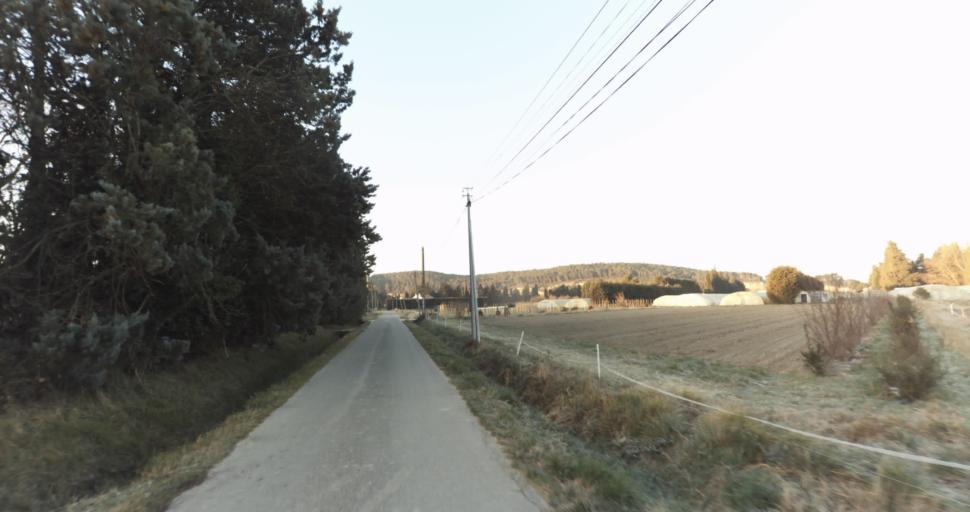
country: FR
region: Provence-Alpes-Cote d'Azur
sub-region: Departement des Bouches-du-Rhone
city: Barbentane
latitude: 43.9026
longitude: 4.7709
